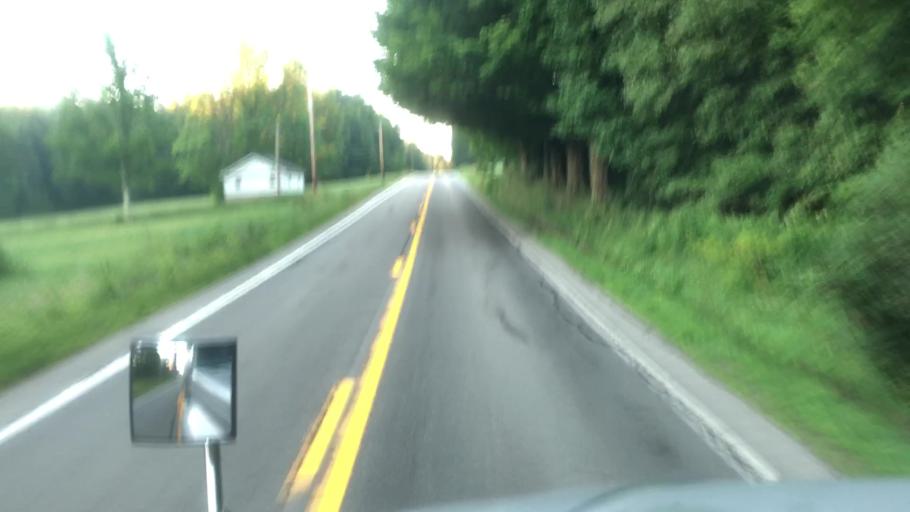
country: US
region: Pennsylvania
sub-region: Crawford County
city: Titusville
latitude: 41.5828
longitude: -79.6098
